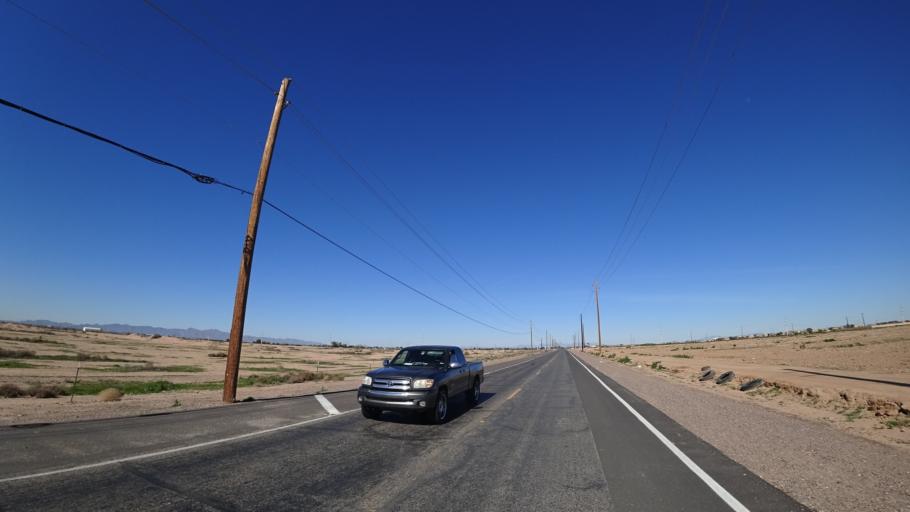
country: US
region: Arizona
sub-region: Maricopa County
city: Tolleson
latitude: 33.4006
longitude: -112.2892
